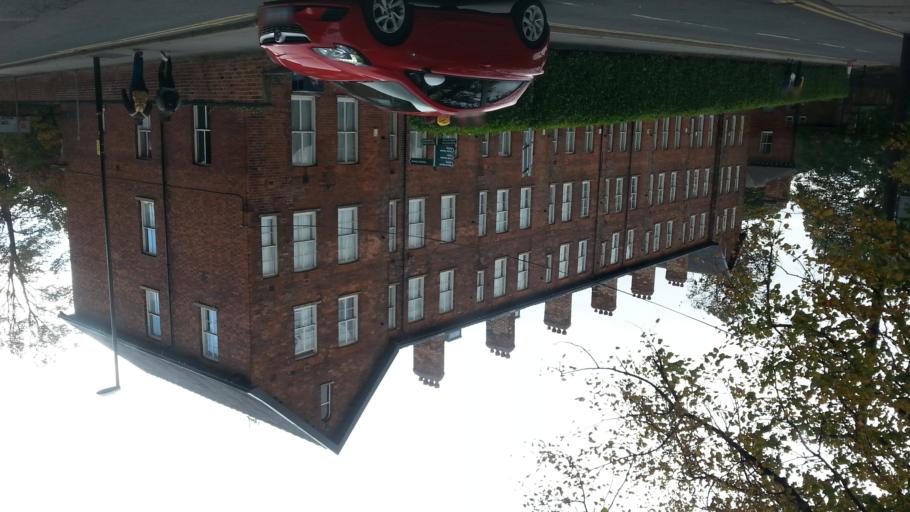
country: GB
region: England
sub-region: City and Borough of Leeds
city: Leeds
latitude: 53.8062
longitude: -1.5604
